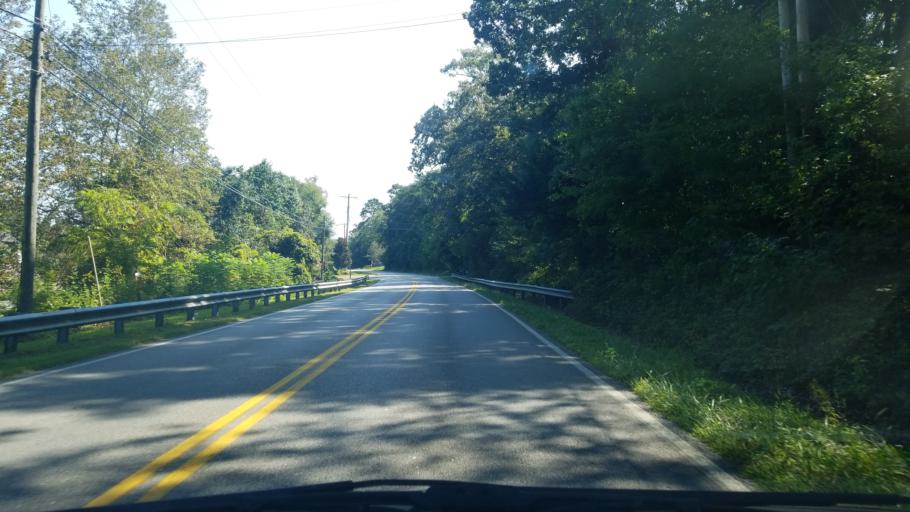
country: US
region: Tennessee
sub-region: Hamilton County
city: Collegedale
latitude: 35.0749
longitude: -85.0872
